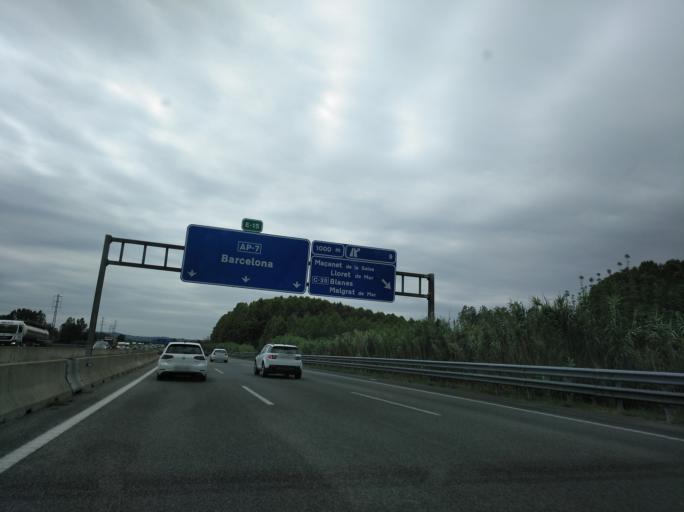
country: ES
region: Catalonia
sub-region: Provincia de Girona
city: Sils
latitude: 41.7978
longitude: 2.7467
